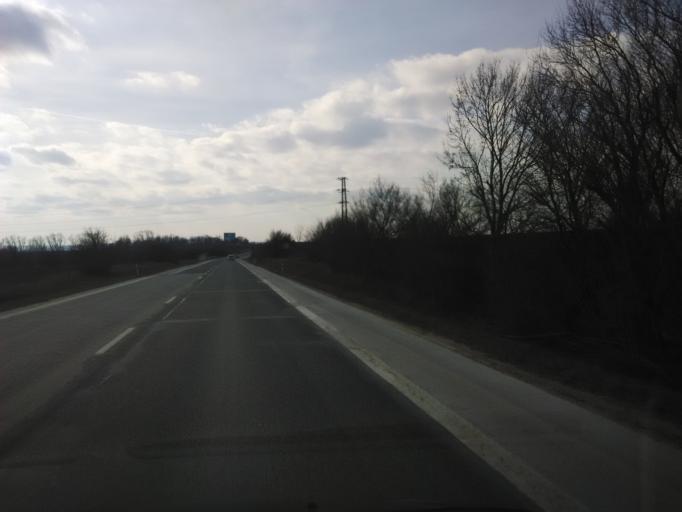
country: SK
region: Nitriansky
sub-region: Okres Nitra
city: Nitra
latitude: 48.3253
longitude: 18.1353
